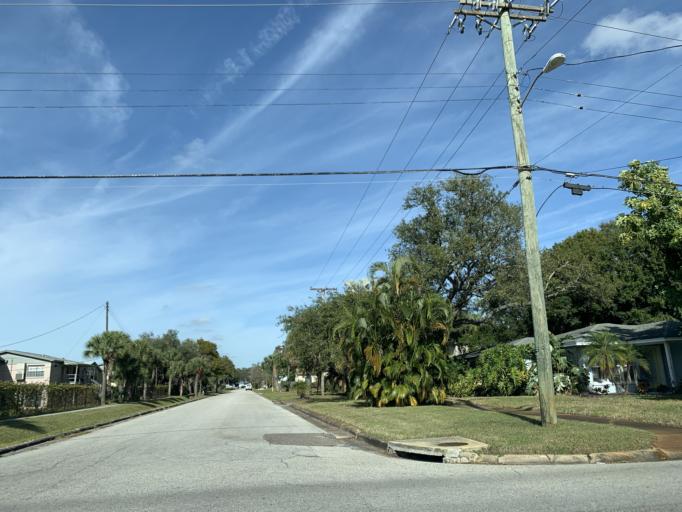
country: US
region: Florida
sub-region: Hillsborough County
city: Tampa
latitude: 27.8899
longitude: -82.5001
